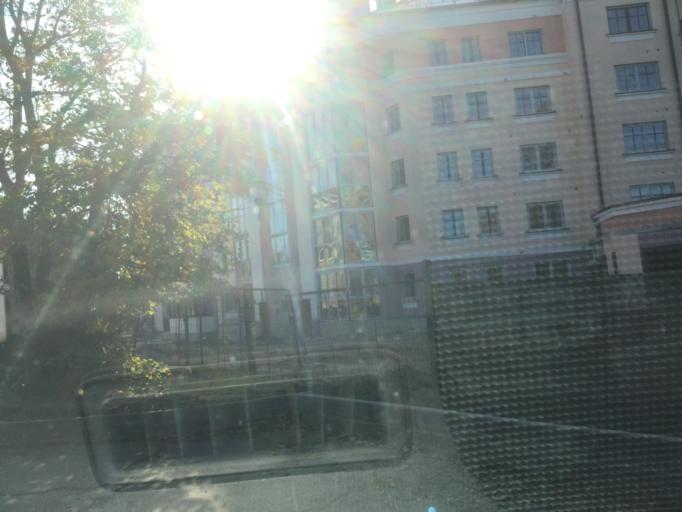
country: BY
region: Vitebsk
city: Vitebsk
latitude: 55.1733
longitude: 30.1954
